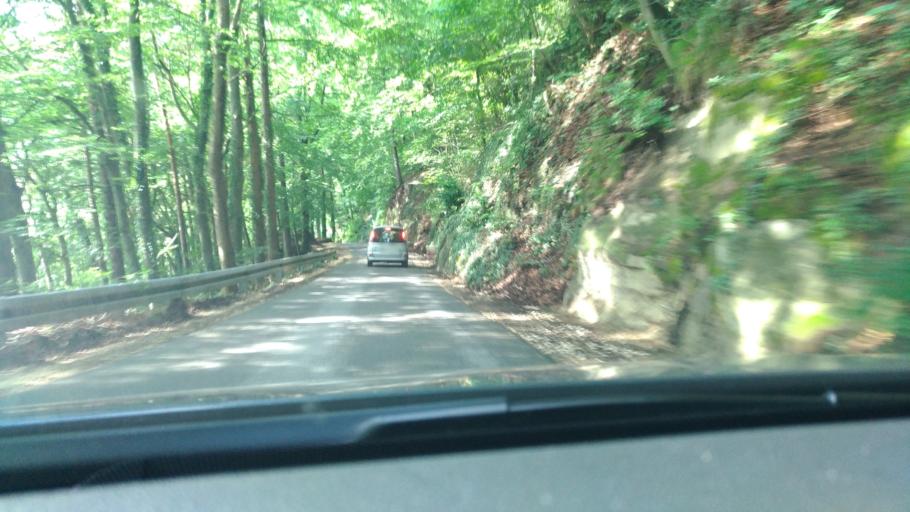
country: DE
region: Baden-Wuerttemberg
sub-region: Tuebingen Region
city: Sipplingen
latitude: 47.7920
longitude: 9.1220
